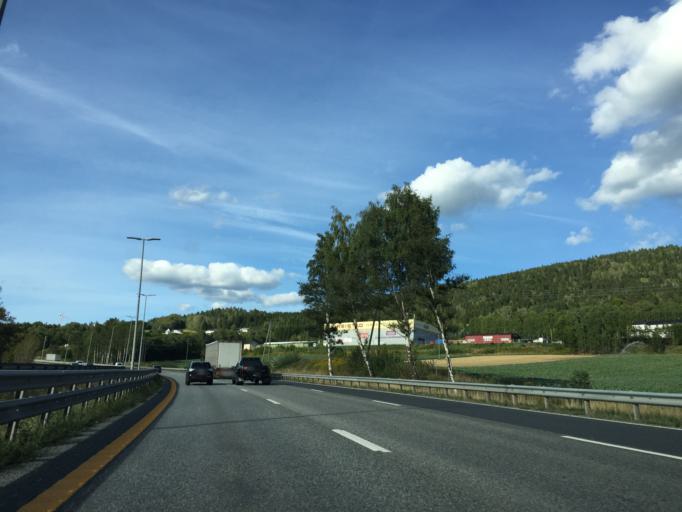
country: NO
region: Buskerud
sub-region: Lier
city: Lierbyen
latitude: 59.7764
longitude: 10.2765
